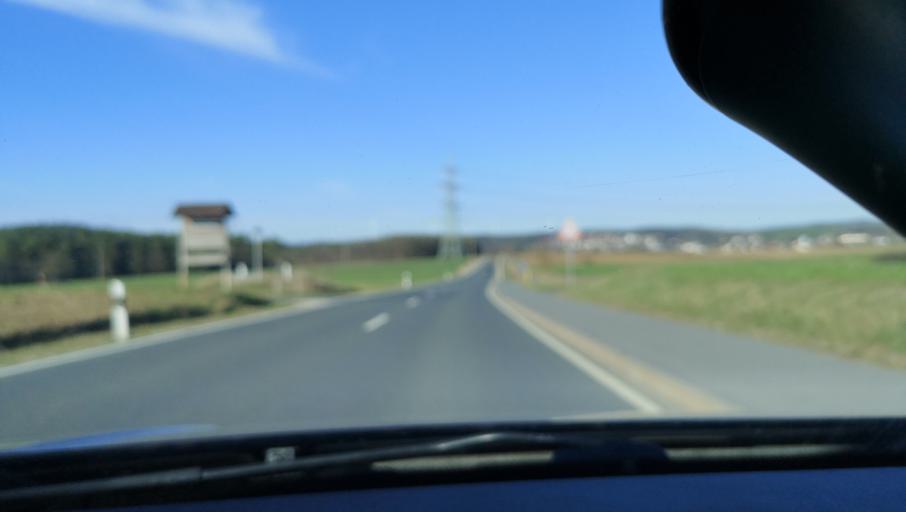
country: DE
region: Bavaria
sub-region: Upper Franconia
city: Sonnefeld
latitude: 50.2095
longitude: 11.1118
